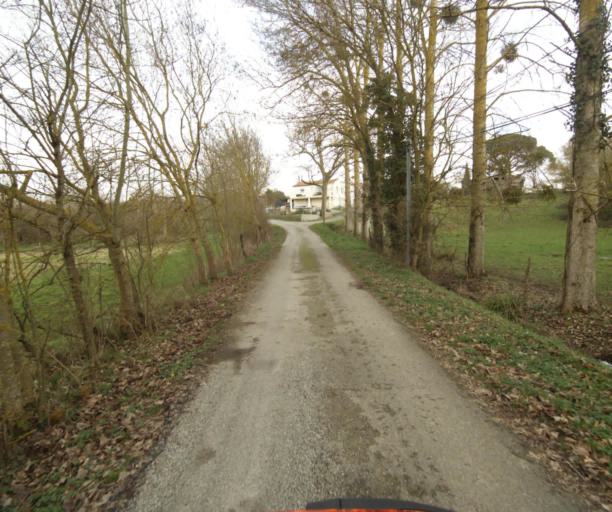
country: FR
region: Languedoc-Roussillon
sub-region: Departement de l'Aude
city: Belpech
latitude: 43.1593
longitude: 1.7013
